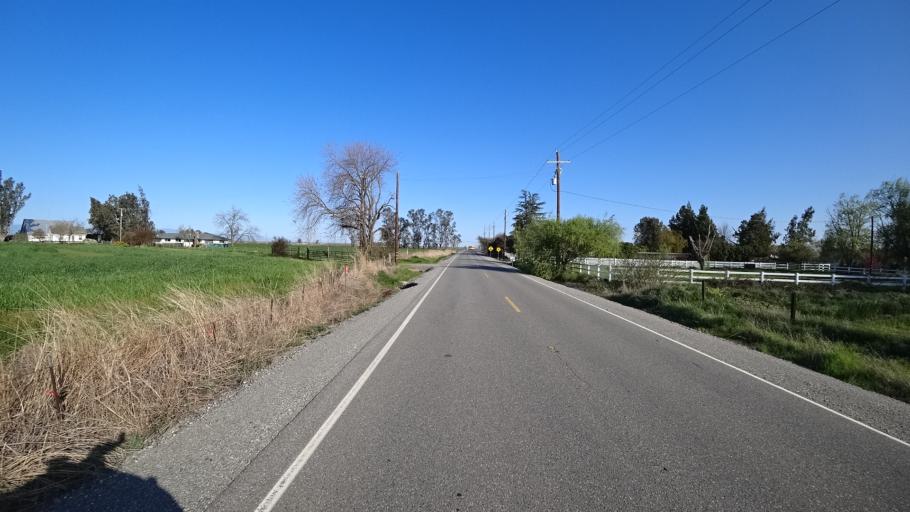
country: US
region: California
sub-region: Glenn County
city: Orland
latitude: 39.7664
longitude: -122.1089
